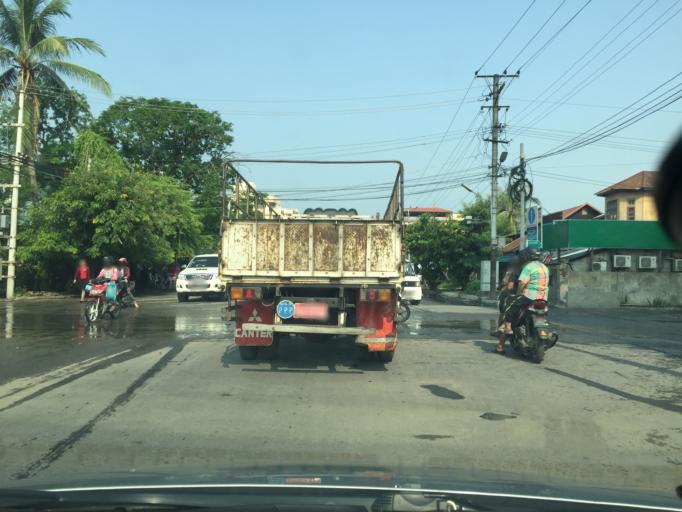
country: MM
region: Mandalay
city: Mandalay
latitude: 21.9710
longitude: 96.0823
